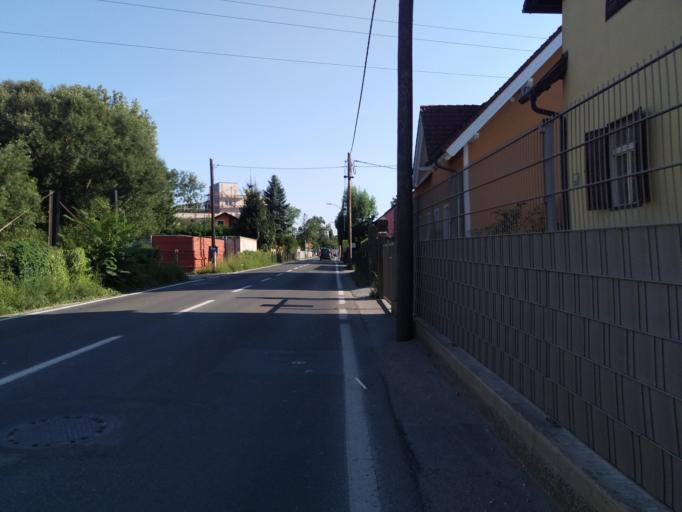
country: AT
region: Styria
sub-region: Politischer Bezirk Graz-Umgebung
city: Feldkirchen bei Graz
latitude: 47.0358
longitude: 15.4401
